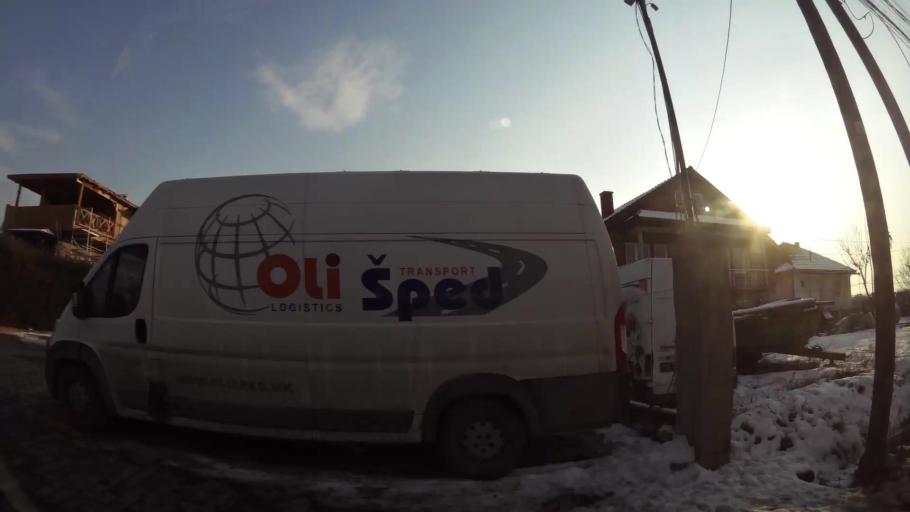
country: MK
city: Creshevo
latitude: 42.0276
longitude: 21.5207
